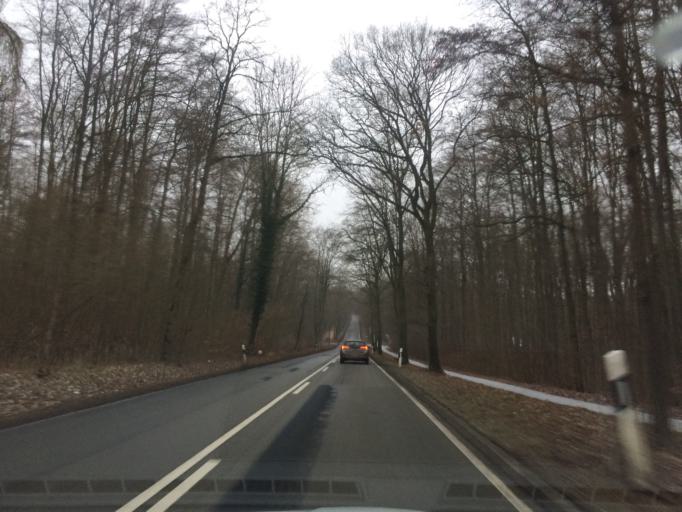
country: DE
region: Hesse
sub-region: Regierungsbezirk Kassel
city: Calden
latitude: 51.3895
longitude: 9.4256
